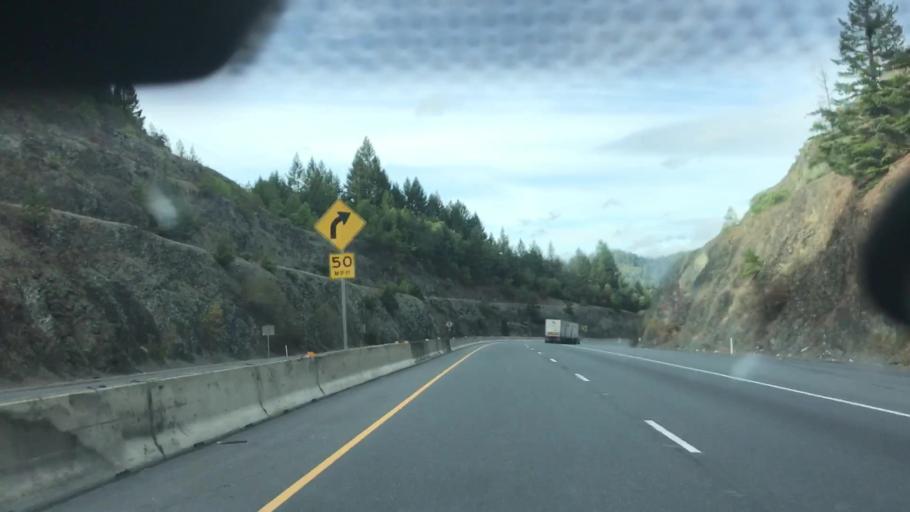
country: US
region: Oregon
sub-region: Douglas County
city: Canyonville
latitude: 42.7323
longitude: -123.3704
